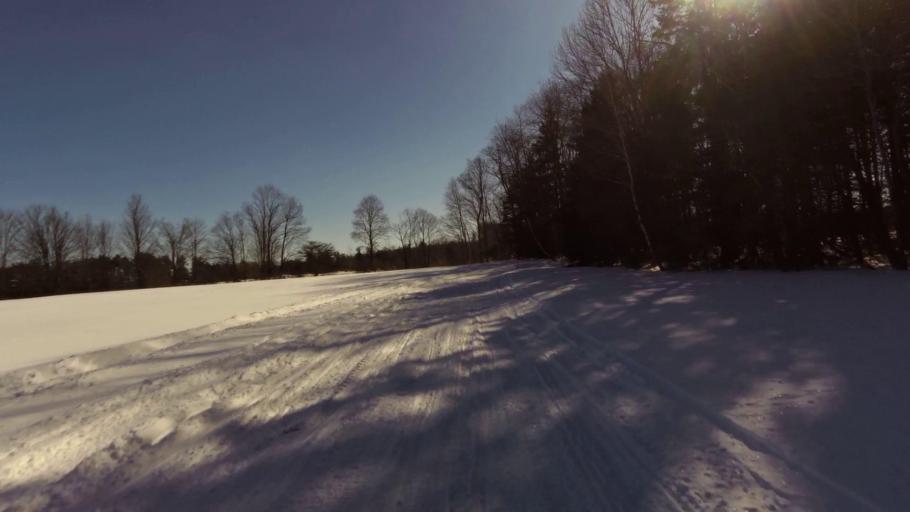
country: US
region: New York
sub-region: Cattaraugus County
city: Franklinville
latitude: 42.4026
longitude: -78.4994
